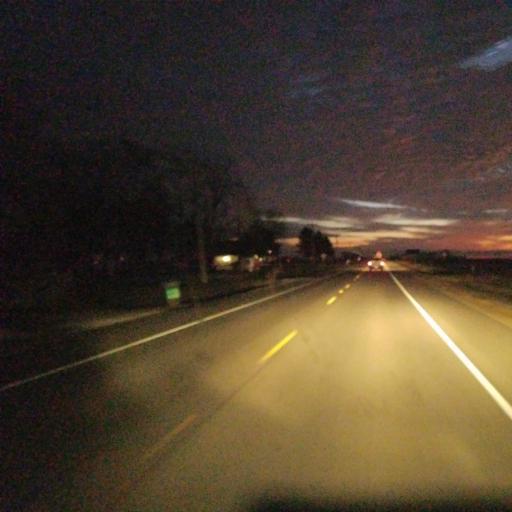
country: US
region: Illinois
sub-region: Peoria County
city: Hanna City
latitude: 40.6974
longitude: -89.8498
